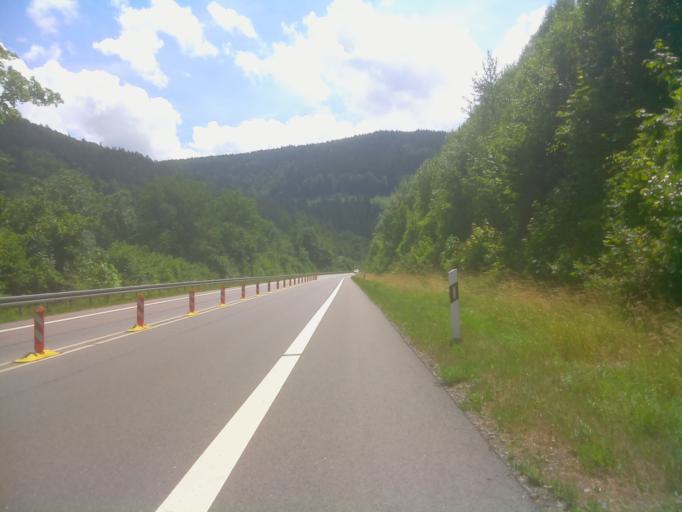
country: DE
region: Hesse
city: Hirschhorn
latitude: 49.4468
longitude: 8.9245
